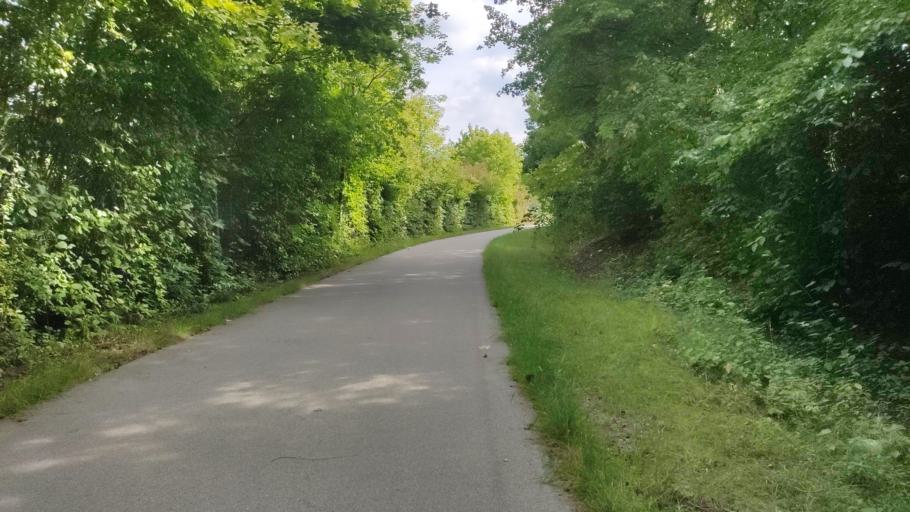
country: DE
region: Bavaria
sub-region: Swabia
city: Kleinaitingen
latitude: 48.2005
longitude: 10.8553
